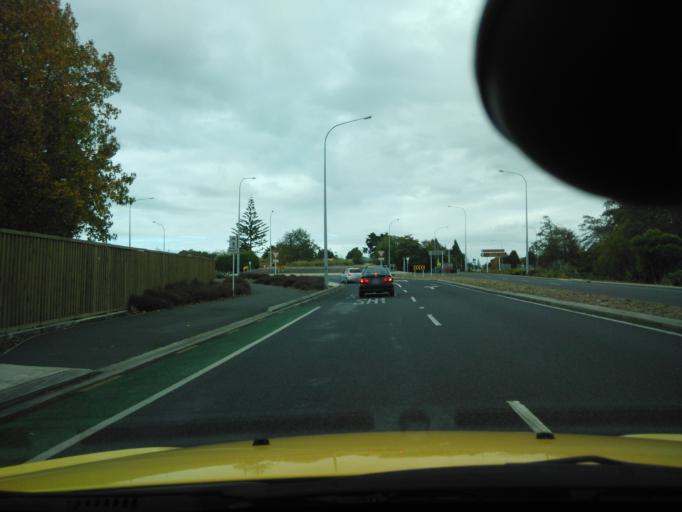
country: NZ
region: Waikato
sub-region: Waikato District
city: Ngaruawahia
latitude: -37.6111
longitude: 175.1860
